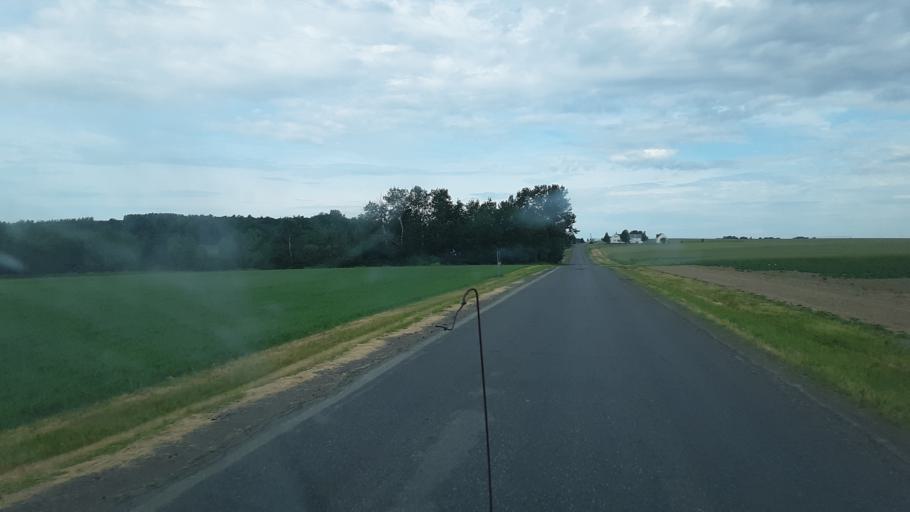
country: US
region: Maine
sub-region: Aroostook County
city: Caribou
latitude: 46.8114
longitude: -68.0065
